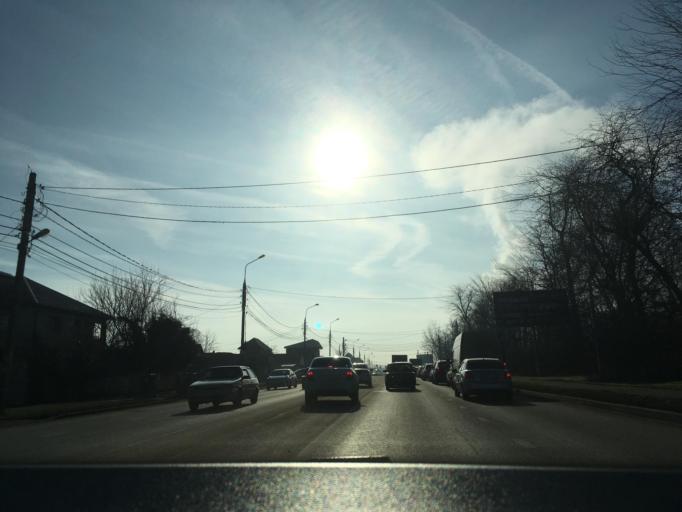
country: RU
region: Krasnodarskiy
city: Krasnodar
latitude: 45.0974
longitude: 39.0134
